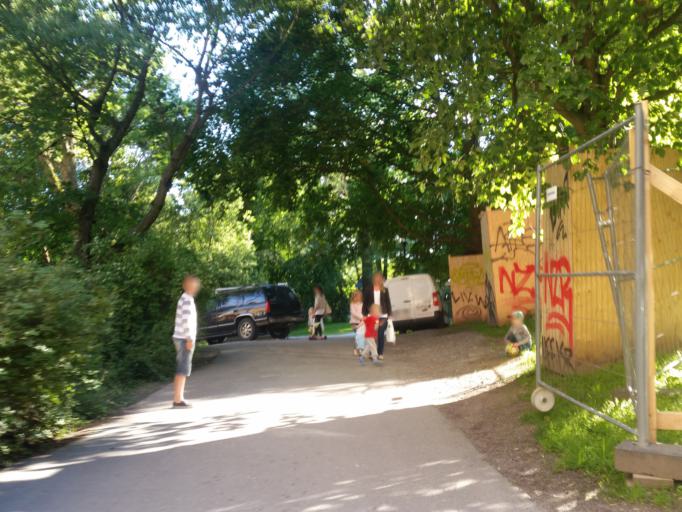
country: SE
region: Stockholm
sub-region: Stockholms Kommun
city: OEstermalm
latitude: 59.3079
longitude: 18.0891
